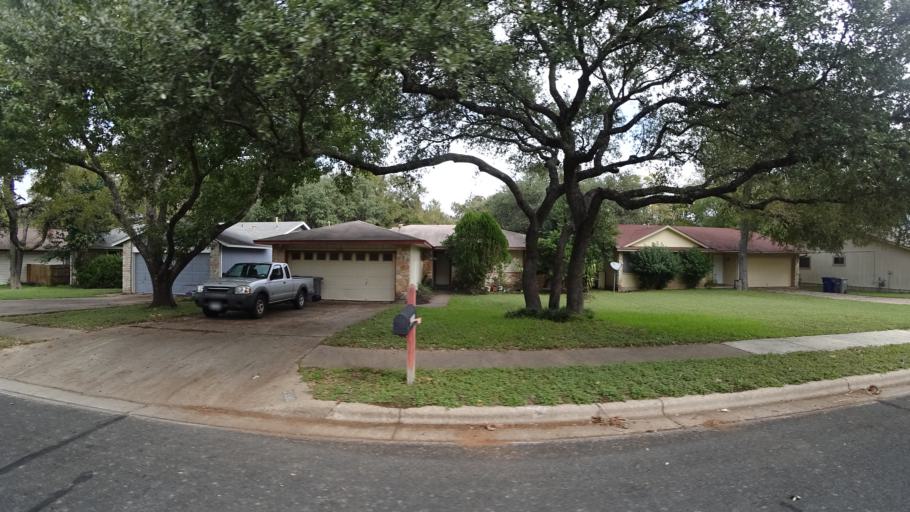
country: US
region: Texas
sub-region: Travis County
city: Shady Hollow
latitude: 30.2061
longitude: -97.8312
